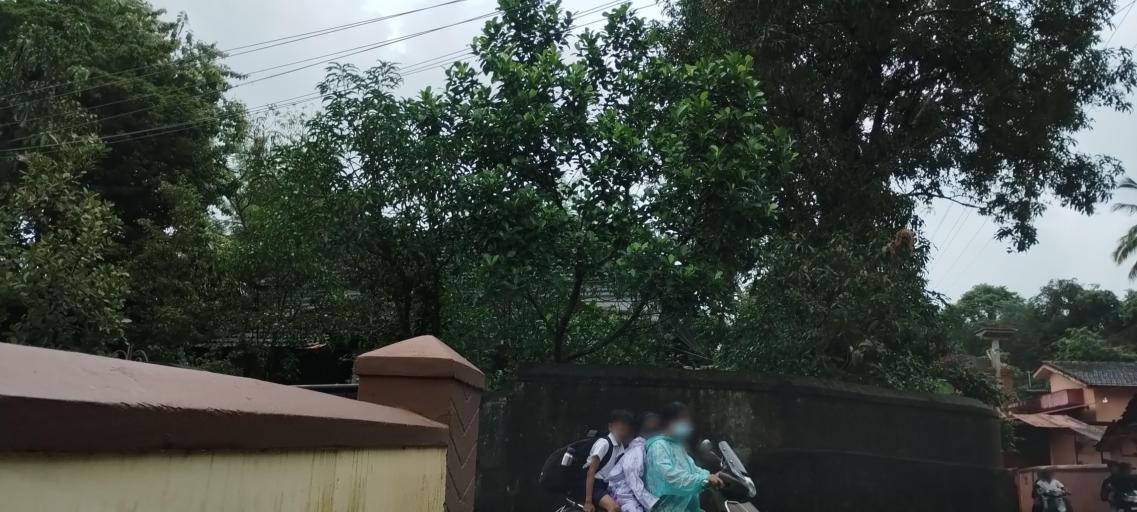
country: IN
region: Goa
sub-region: North Goa
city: Aldona
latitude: 15.5855
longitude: 73.8679
